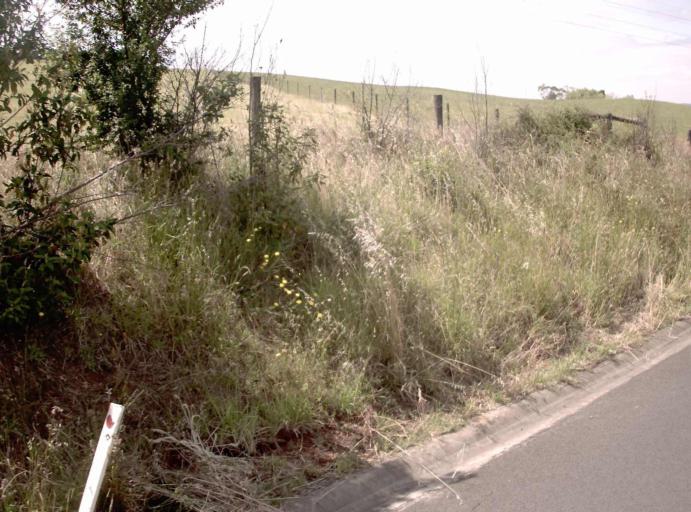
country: AU
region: Victoria
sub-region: Baw Baw
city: Warragul
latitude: -38.4514
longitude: 145.9777
